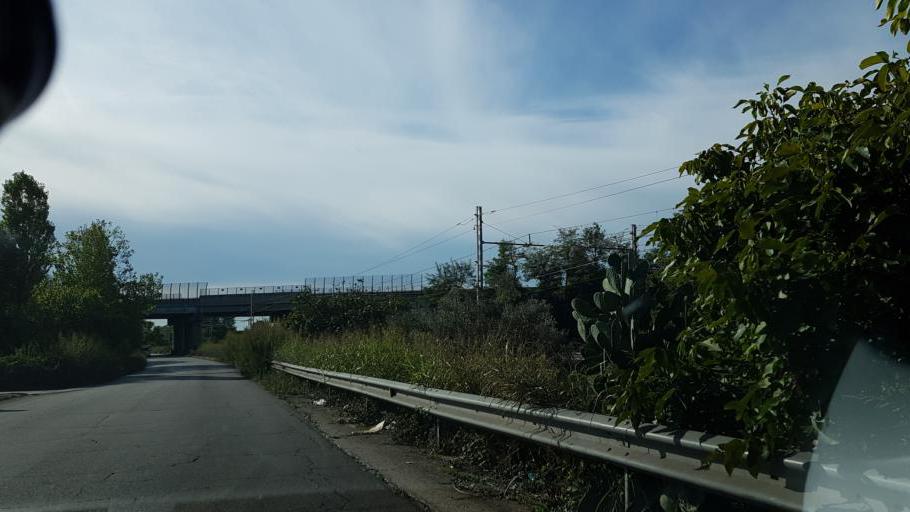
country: IT
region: Apulia
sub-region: Provincia di Brindisi
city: La Rosa
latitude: 40.6188
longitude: 17.9510
